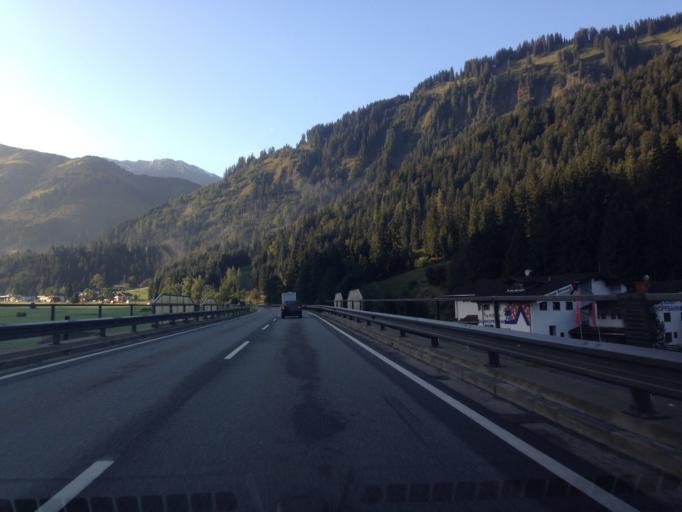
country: AT
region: Tyrol
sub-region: Politischer Bezirk Reutte
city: Bichlbach
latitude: 47.4283
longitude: 10.7772
